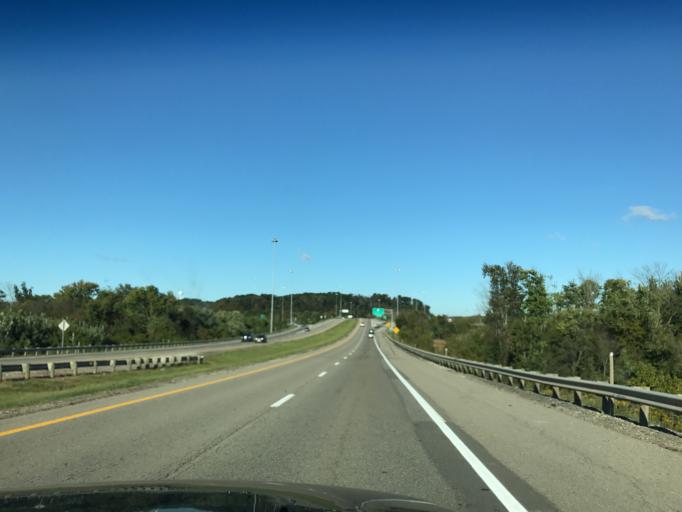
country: US
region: West Virginia
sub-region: Wood County
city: Parkersburg
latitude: 39.2567
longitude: -81.5489
